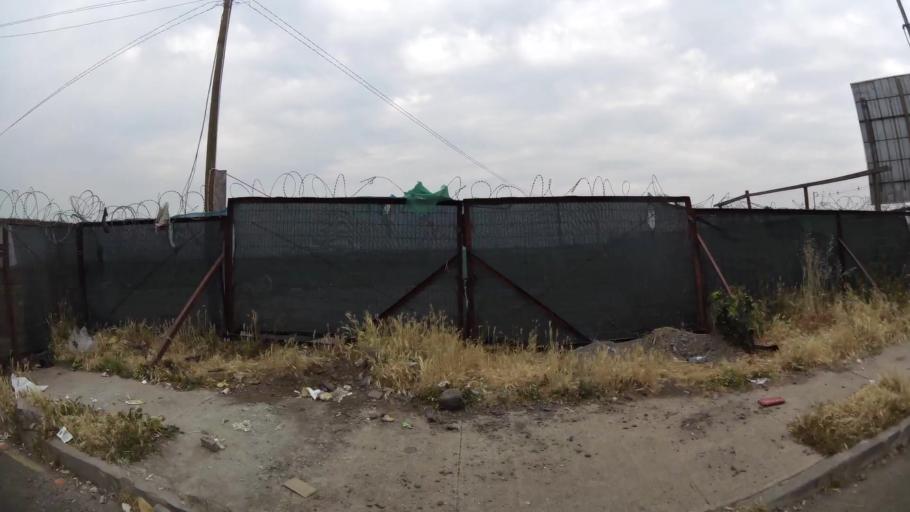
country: CL
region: Santiago Metropolitan
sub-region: Provincia de Chacabuco
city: Chicureo Abajo
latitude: -33.1953
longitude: -70.6670
